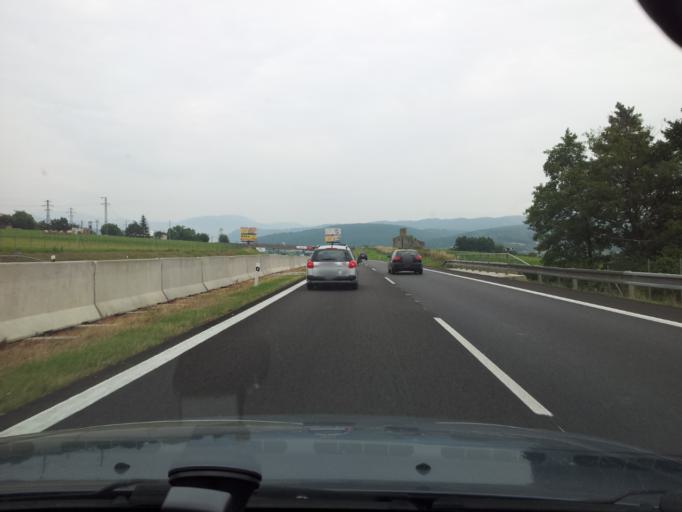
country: SK
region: Banskobystricky
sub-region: Okres Banska Bystrica
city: Banska Bystrica
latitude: 48.6619
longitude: 19.1317
